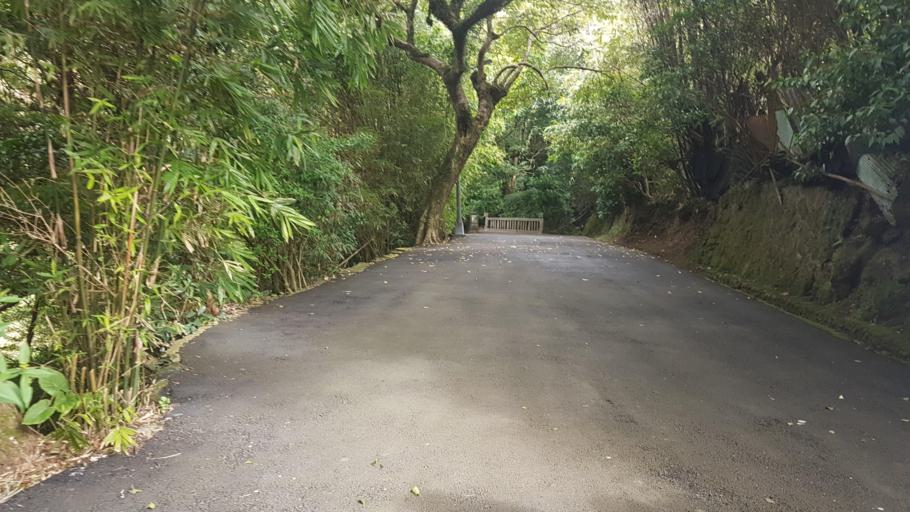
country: TW
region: Taipei
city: Taipei
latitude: 25.1559
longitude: 121.5406
